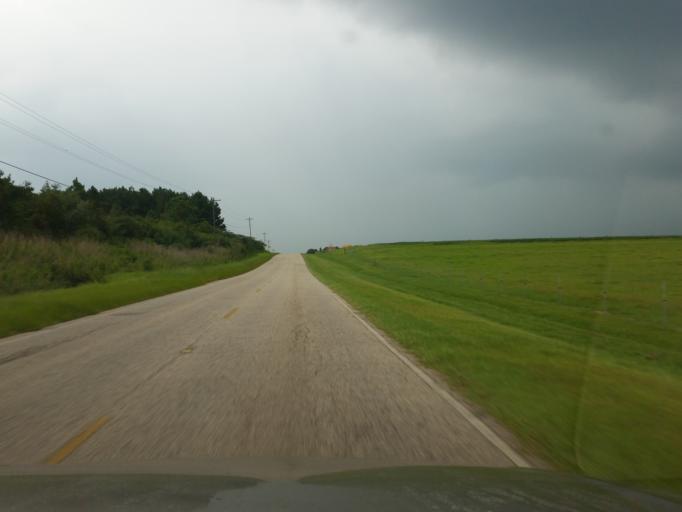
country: US
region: Alabama
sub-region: Baldwin County
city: Robertsdale
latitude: 30.5614
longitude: -87.5815
